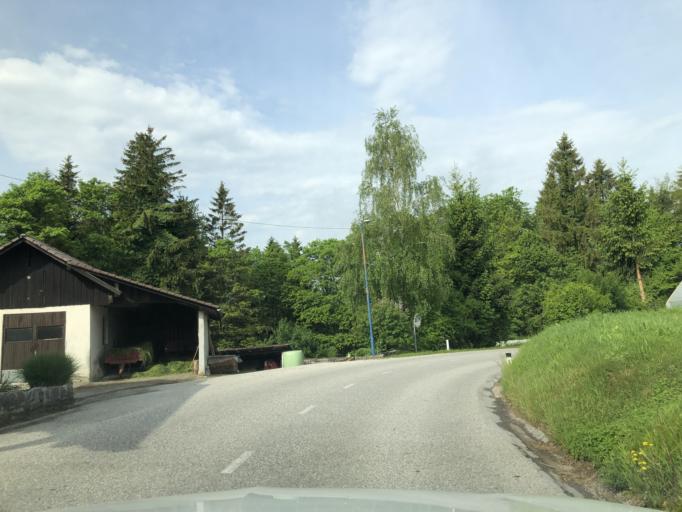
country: SI
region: Velike Lasce
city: Velike Lasce
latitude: 45.8085
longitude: 14.6251
